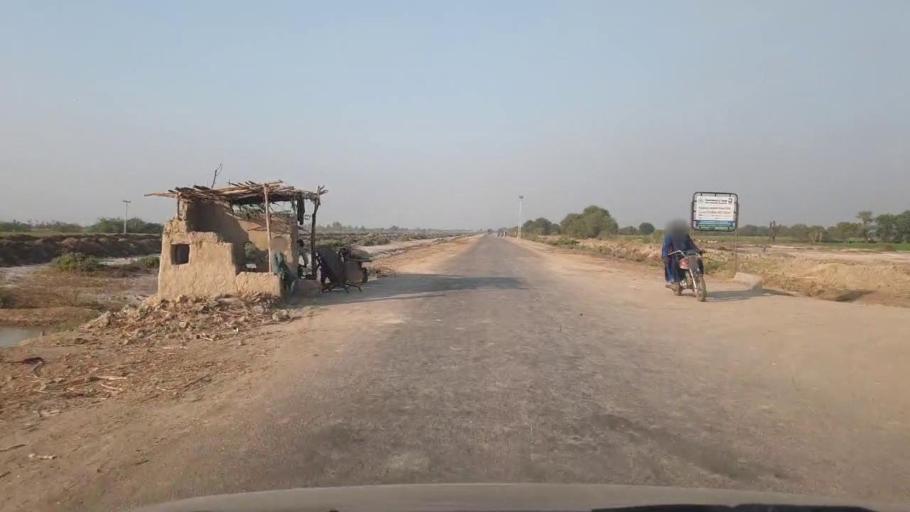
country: PK
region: Sindh
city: Mirwah Gorchani
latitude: 25.3555
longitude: 69.1741
